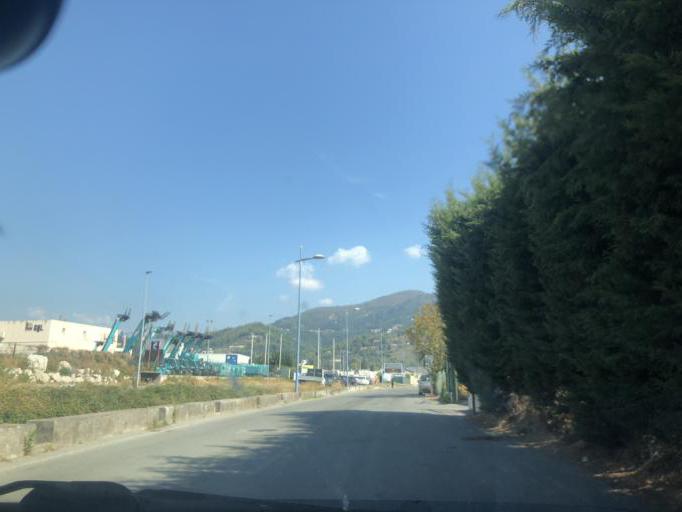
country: FR
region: Provence-Alpes-Cote d'Azur
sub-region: Departement des Alpes-Maritimes
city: Colomars
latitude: 43.7772
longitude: 7.2096
